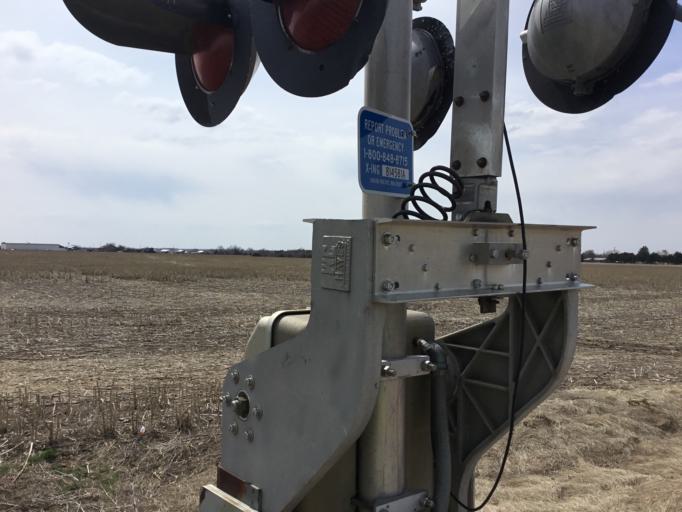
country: US
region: Kansas
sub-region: Russell County
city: Russell
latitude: 38.8928
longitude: -98.8284
